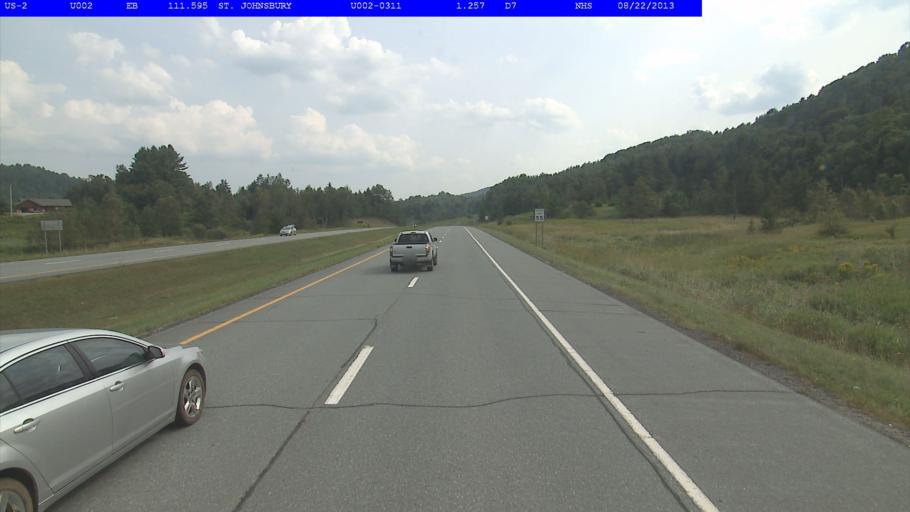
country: US
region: Vermont
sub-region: Caledonia County
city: St Johnsbury
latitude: 44.4366
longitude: -72.0419
